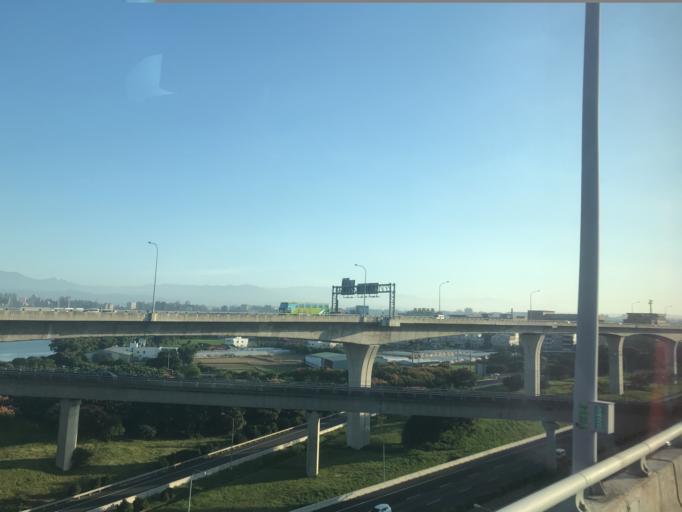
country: TW
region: Taiwan
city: Taoyuan City
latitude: 25.0191
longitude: 121.2731
